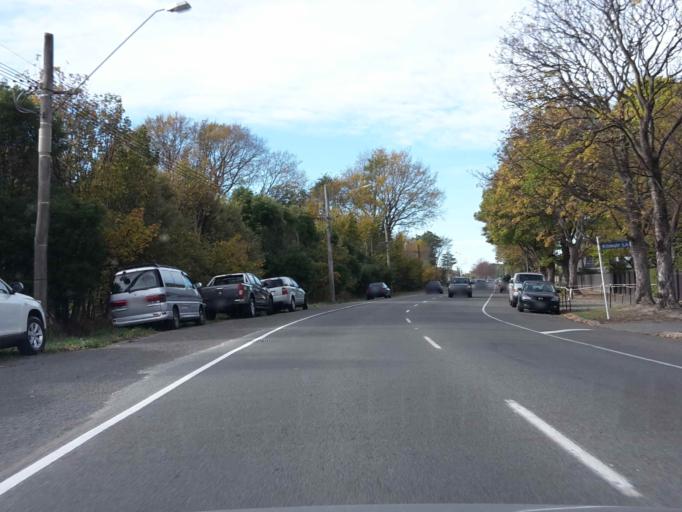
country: NZ
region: Canterbury
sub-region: Christchurch City
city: Christchurch
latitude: -43.4812
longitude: 172.5715
